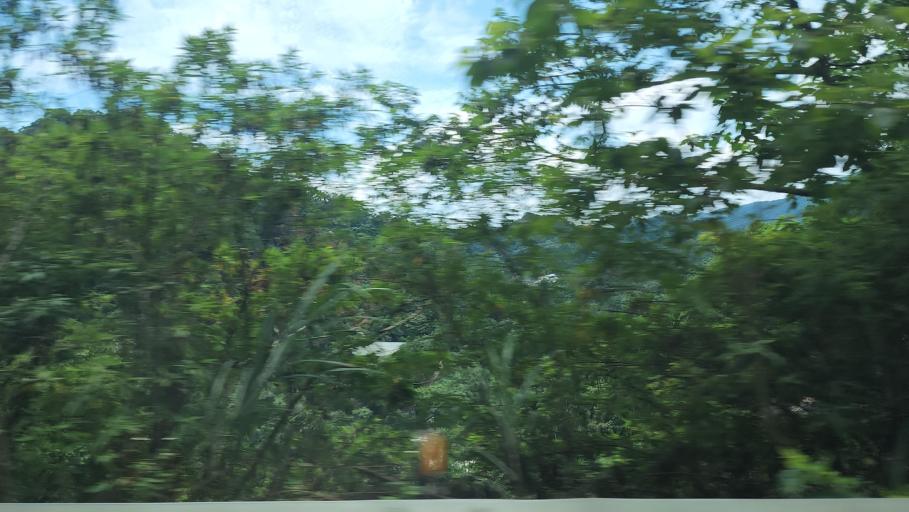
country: TW
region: Taipei
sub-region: Taipei
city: Banqiao
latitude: 24.9048
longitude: 121.4336
